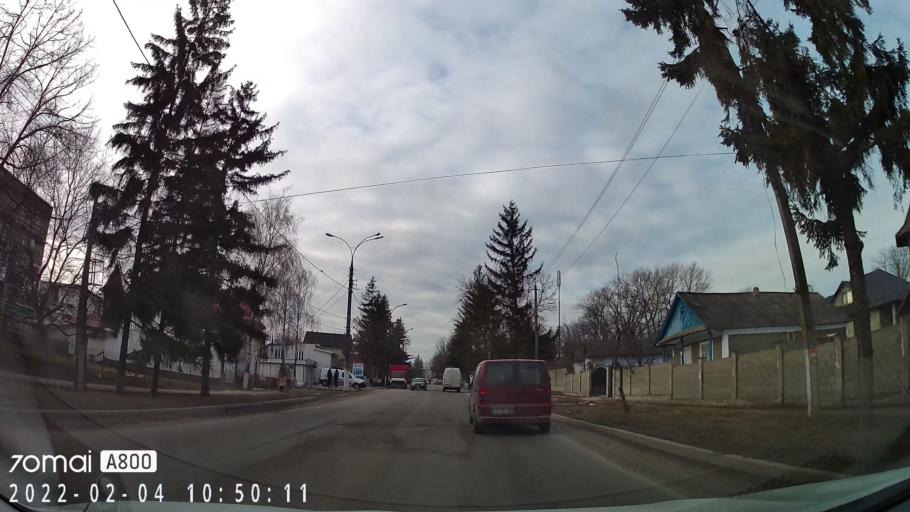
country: MD
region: Briceni
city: Briceni
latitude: 48.3552
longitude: 27.0870
